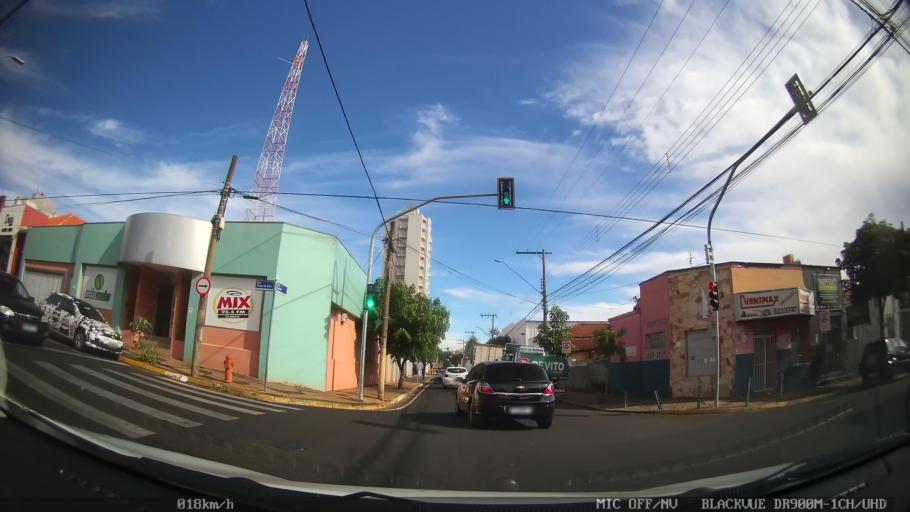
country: BR
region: Sao Paulo
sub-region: Catanduva
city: Catanduva
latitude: -21.1380
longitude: -48.9753
